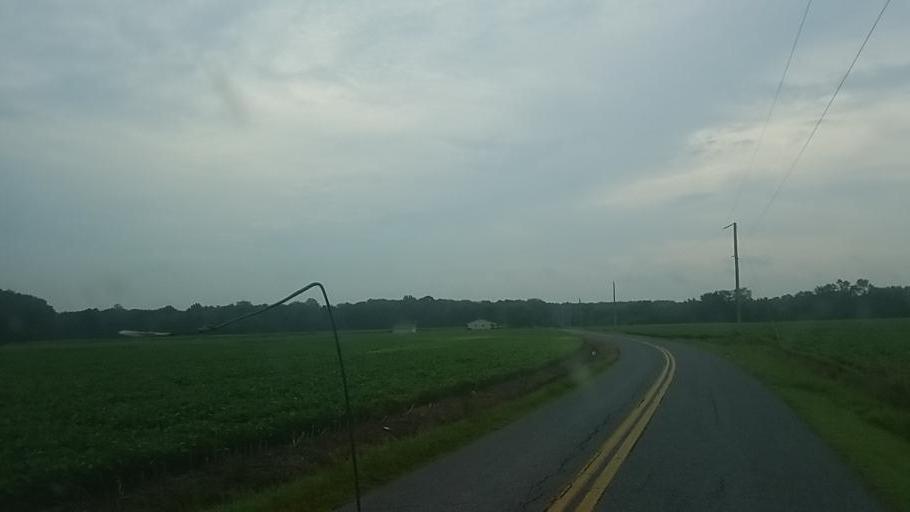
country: US
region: Delaware
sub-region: Sussex County
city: Selbyville
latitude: 38.4440
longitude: -75.2084
